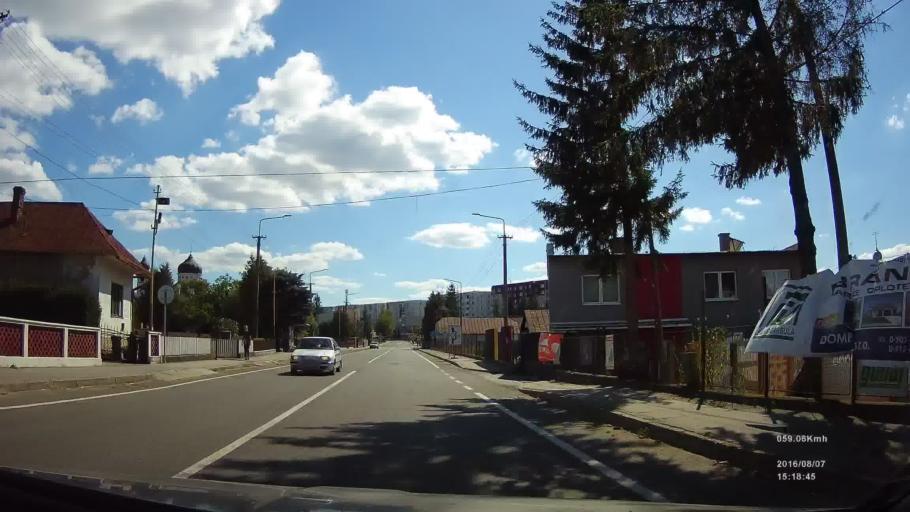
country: SK
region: Presovsky
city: Stropkov
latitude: 49.2085
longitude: 21.6527
